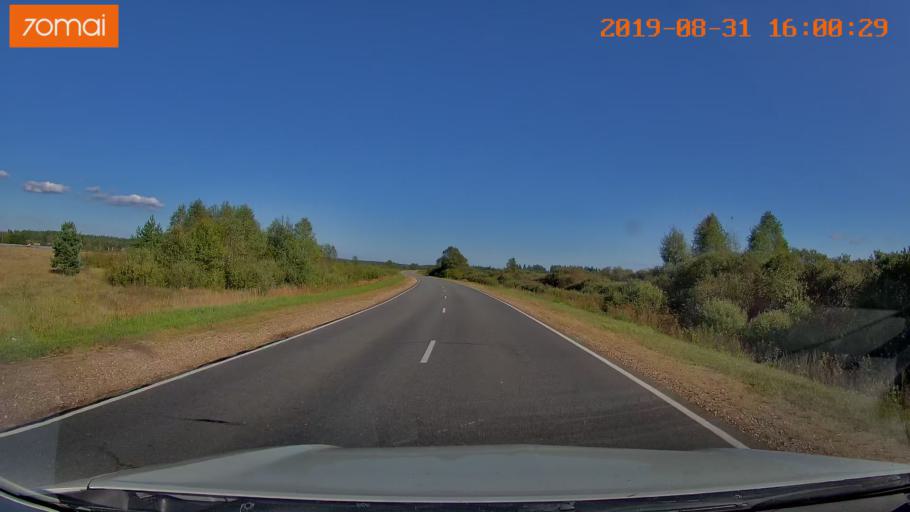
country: RU
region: Kaluga
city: Yukhnov
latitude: 54.7002
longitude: 35.2751
